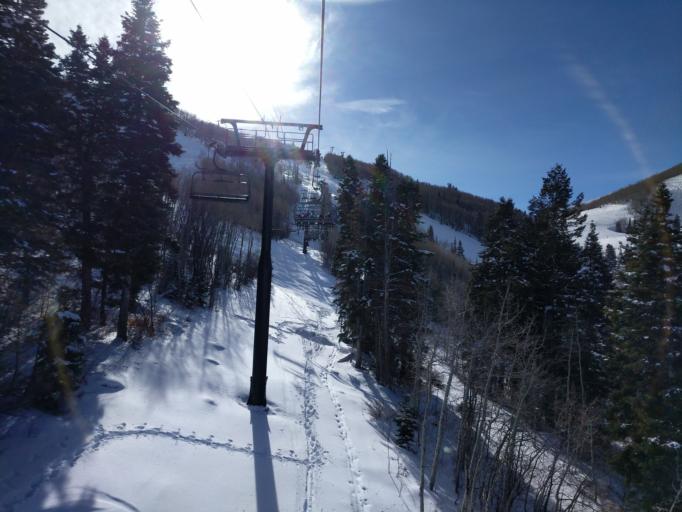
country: US
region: Utah
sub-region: Summit County
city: Park City
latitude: 40.6409
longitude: -111.5081
